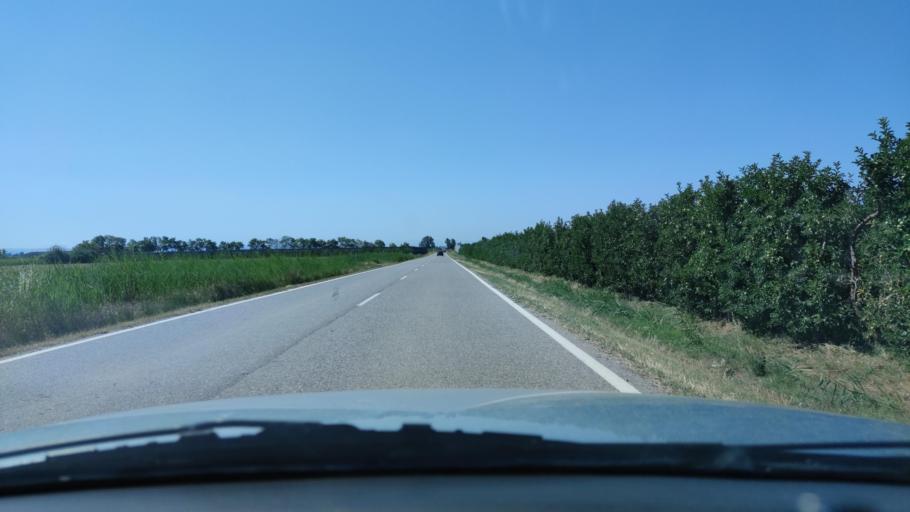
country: ES
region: Catalonia
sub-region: Provincia de Lleida
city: Penelles
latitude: 41.7235
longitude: 0.9827
